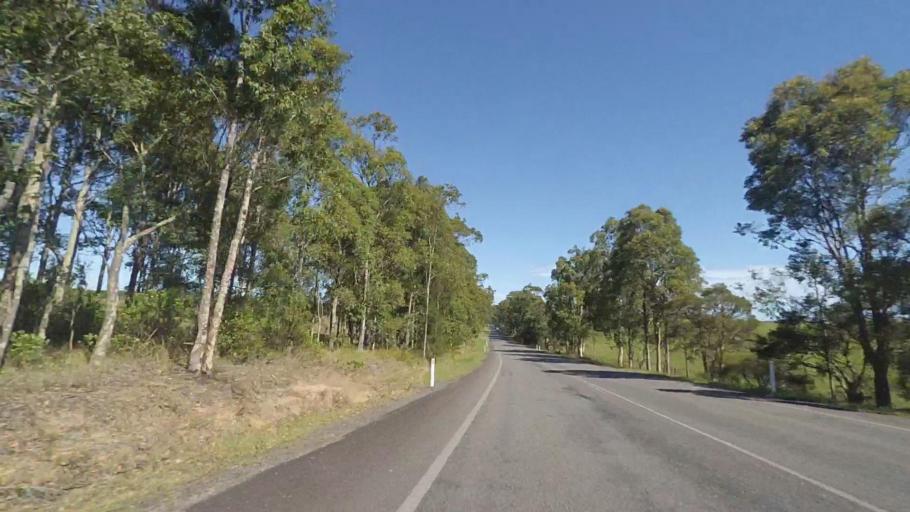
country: AU
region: New South Wales
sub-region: Great Lakes
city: Hawks Nest
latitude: -32.6290
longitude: 152.1340
